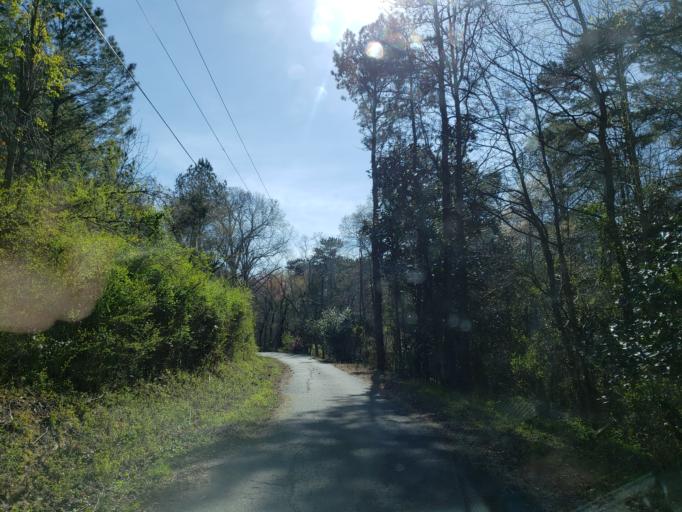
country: US
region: Georgia
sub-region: Cobb County
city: Marietta
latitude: 33.9934
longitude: -84.4707
